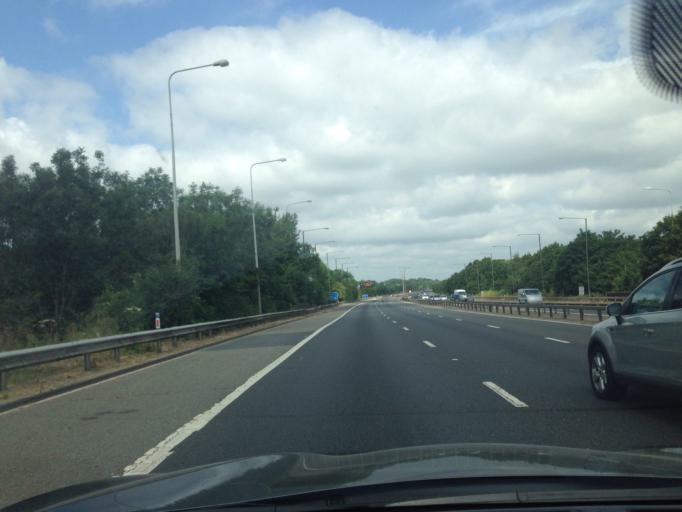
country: GB
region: England
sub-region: Hertfordshire
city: Elstree
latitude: 51.6370
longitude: -0.3084
